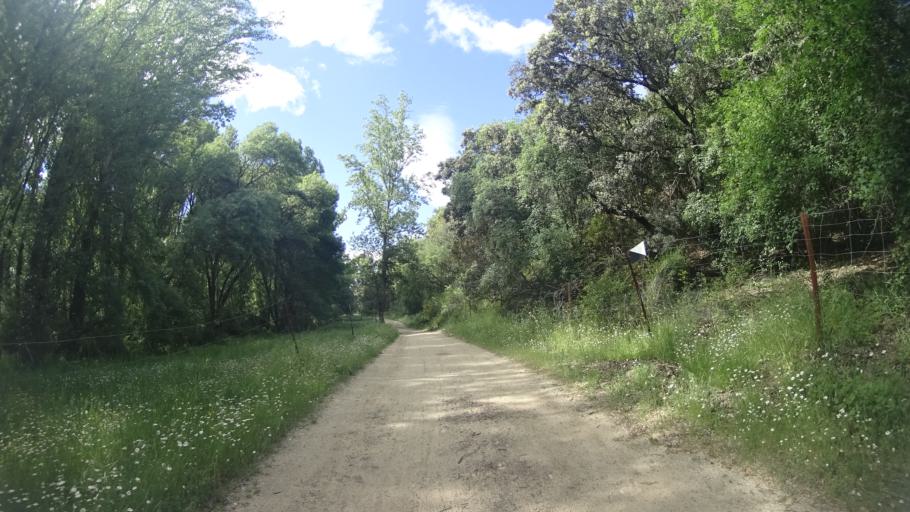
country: ES
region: Madrid
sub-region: Provincia de Madrid
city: Brunete
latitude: 40.4282
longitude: -3.9532
